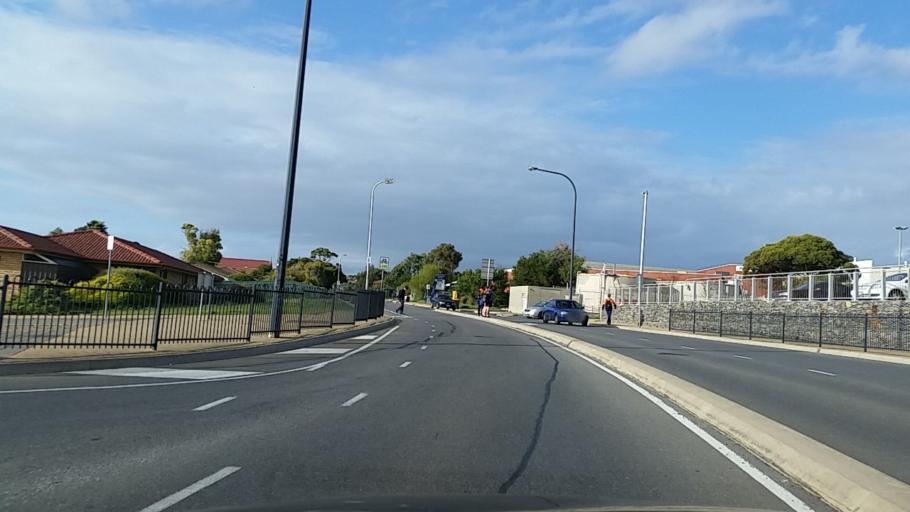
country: AU
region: South Australia
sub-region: Marion
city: Happy Valley
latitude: -35.0773
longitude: 138.5148
